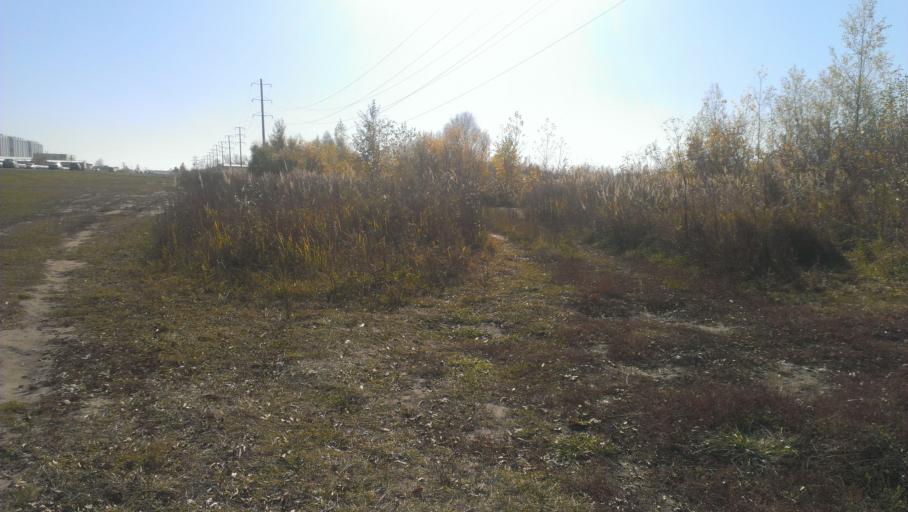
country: RU
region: Altai Krai
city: Novosilikatnyy
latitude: 53.3440
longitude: 83.6348
